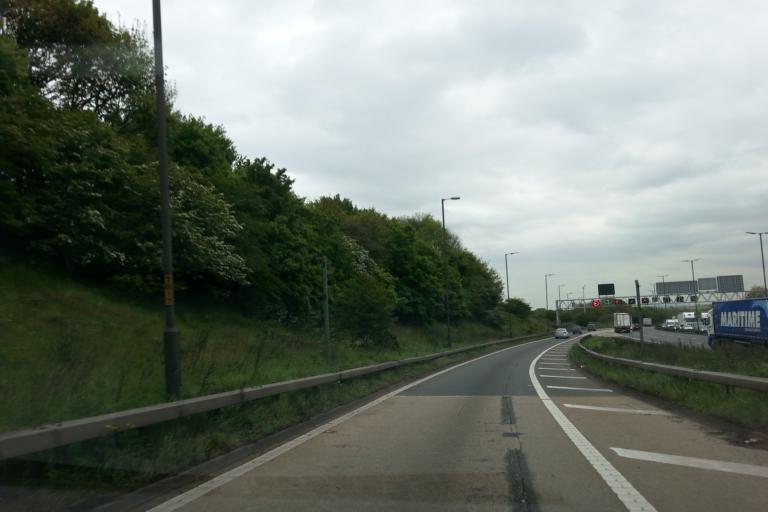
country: GB
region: England
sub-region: Walsall
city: Aldridge
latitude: 52.5533
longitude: -1.9295
